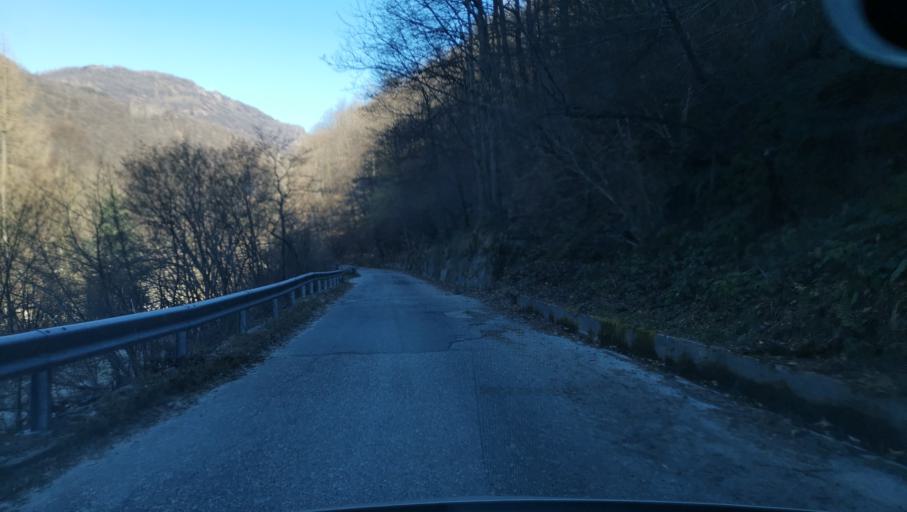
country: IT
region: Piedmont
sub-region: Provincia di Torino
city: Rora
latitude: 44.7773
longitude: 7.2077
